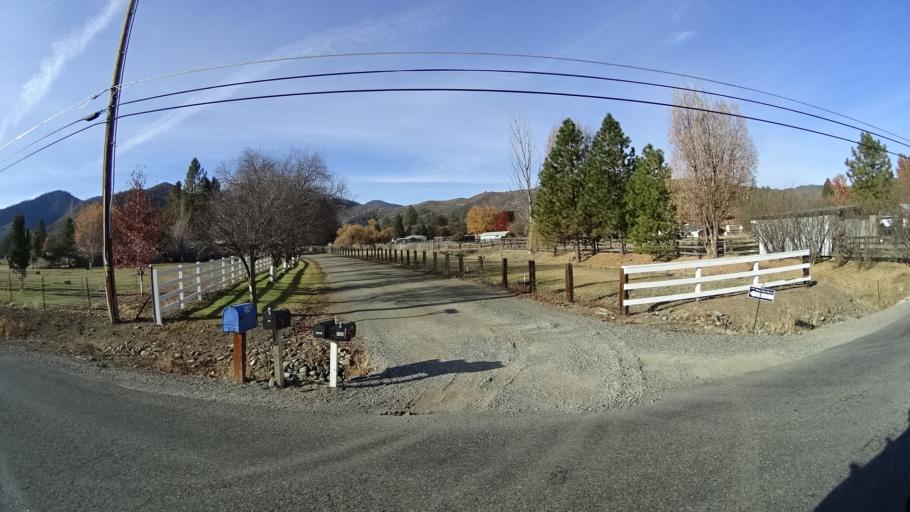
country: US
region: California
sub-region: Siskiyou County
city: Yreka
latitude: 41.6809
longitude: -122.6348
